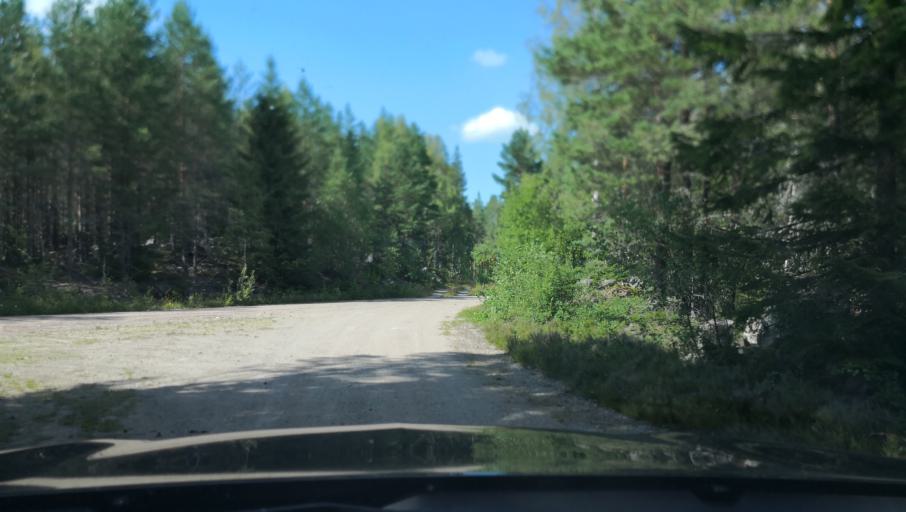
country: SE
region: Vaestmanland
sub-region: Vasteras
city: Skultuna
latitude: 59.7116
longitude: 16.3700
